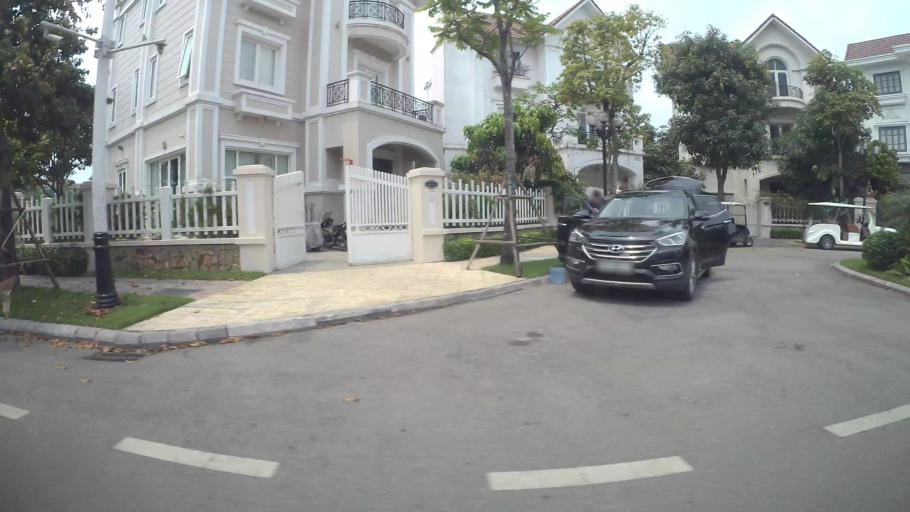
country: VN
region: Ha Noi
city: Trau Quy
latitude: 21.0430
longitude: 105.9156
